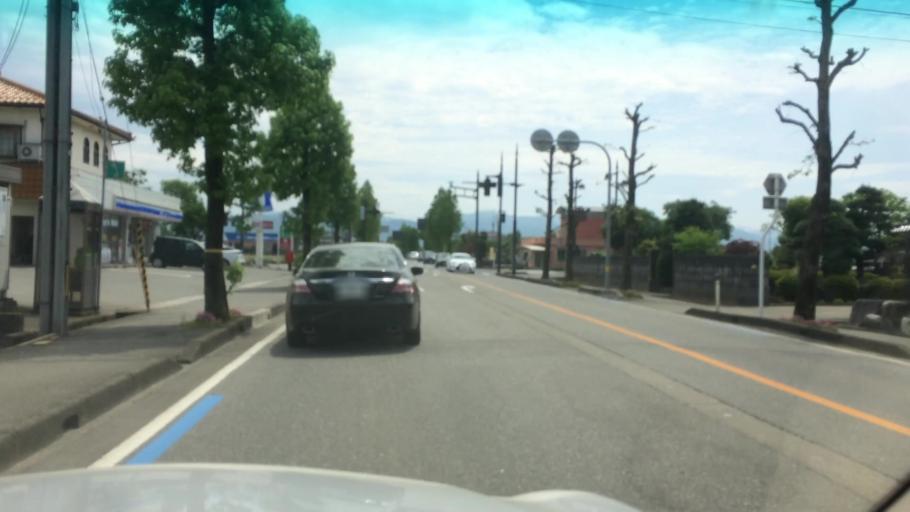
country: JP
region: Toyama
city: Toyama-shi
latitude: 36.6440
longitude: 137.1938
